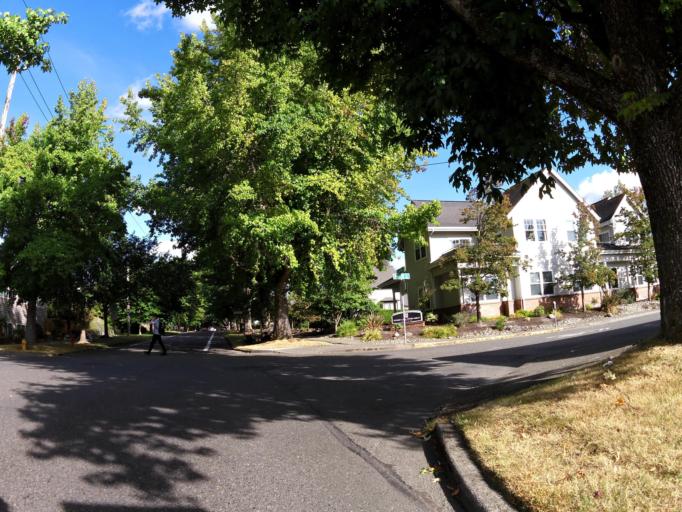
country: US
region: Washington
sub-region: Thurston County
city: Olympia
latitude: 47.0439
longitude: -122.8913
